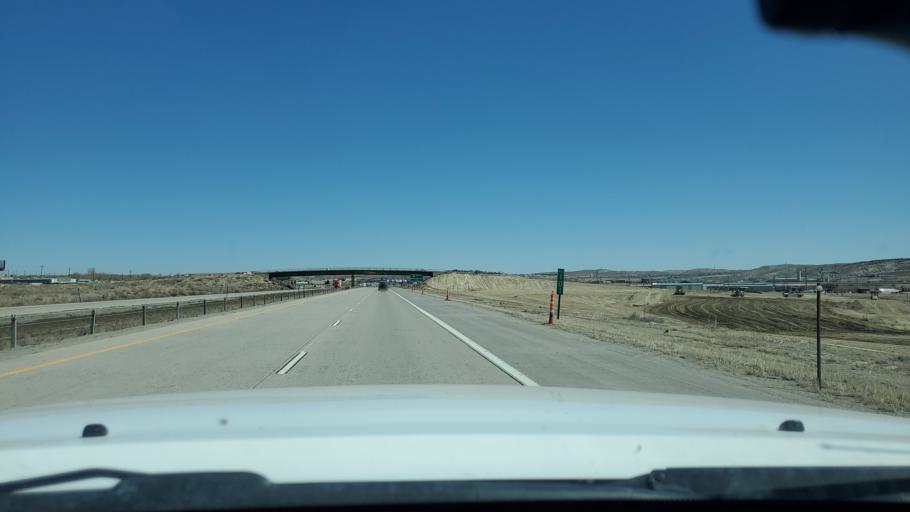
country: US
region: Wyoming
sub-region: Sweetwater County
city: North Rock Springs
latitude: 41.5702
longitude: -109.2793
